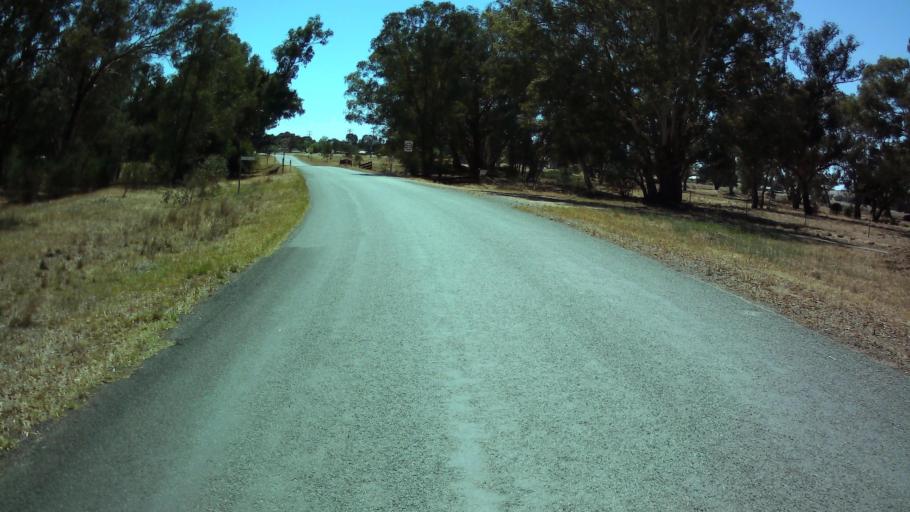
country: AU
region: New South Wales
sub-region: Weddin
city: Grenfell
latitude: -33.9996
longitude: 148.3979
